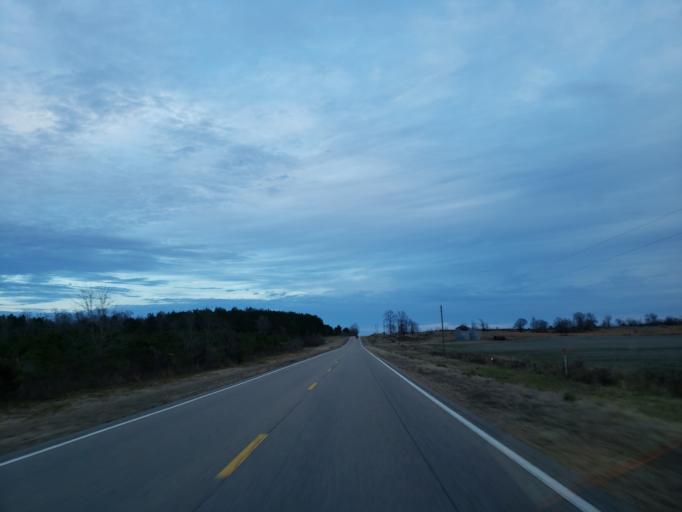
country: US
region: Mississippi
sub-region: Kemper County
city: De Kalb
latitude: 32.8309
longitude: -88.3937
